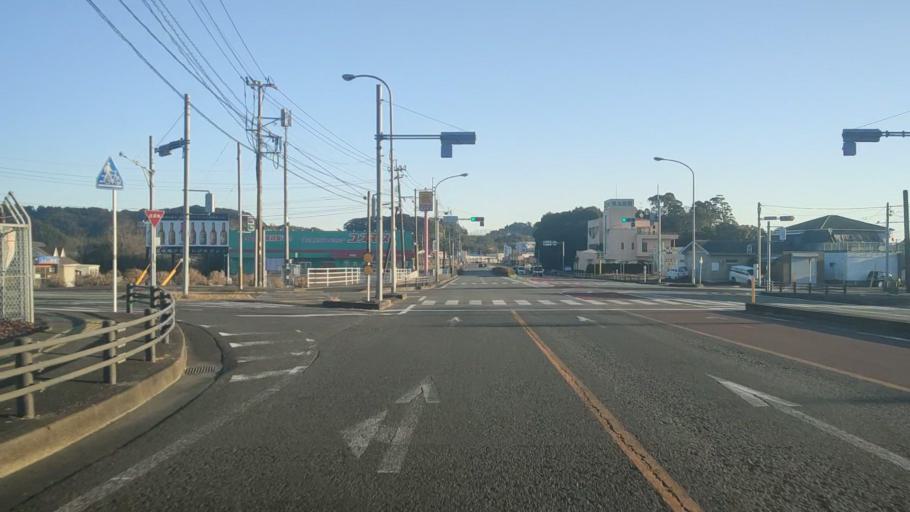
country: JP
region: Miyazaki
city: Takanabe
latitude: 32.0703
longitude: 131.4906
